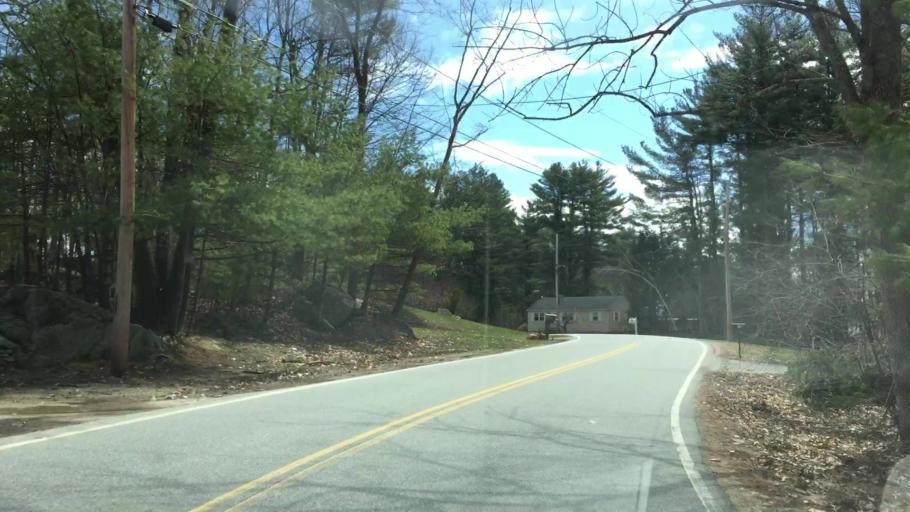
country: US
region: New Hampshire
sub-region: Hillsborough County
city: Pelham
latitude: 42.7144
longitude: -71.3457
